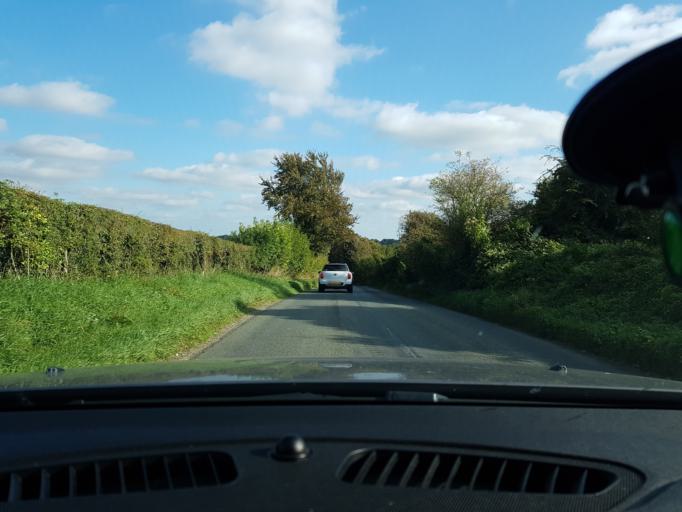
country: GB
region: England
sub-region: Wiltshire
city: Aldbourne
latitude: 51.5083
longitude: -1.6187
